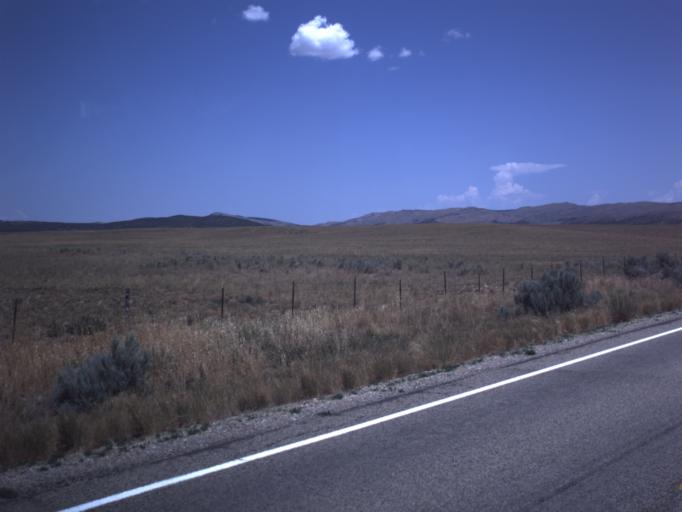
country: US
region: Utah
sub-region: Juab County
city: Nephi
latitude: 39.6852
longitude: -112.0078
